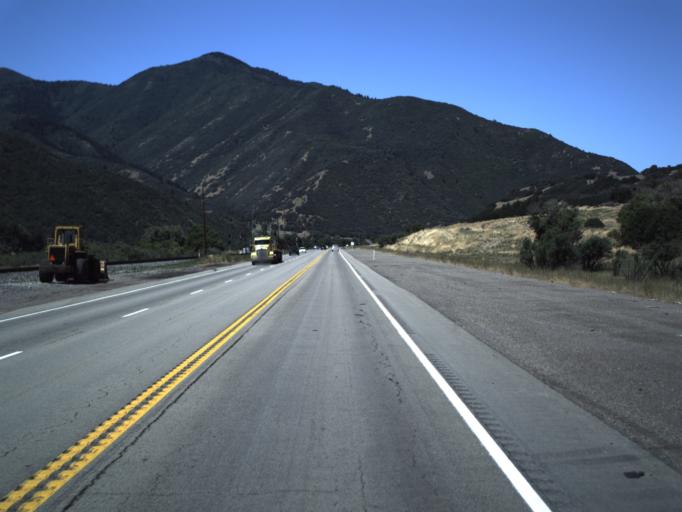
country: US
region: Utah
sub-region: Utah County
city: Mapleton
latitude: 40.0366
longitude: -111.5294
